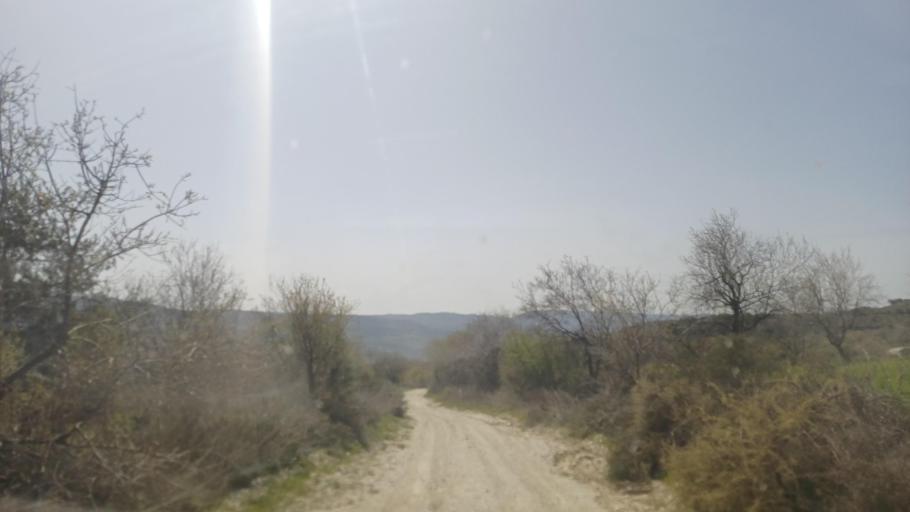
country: CY
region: Limassol
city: Pachna
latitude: 34.8695
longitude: 32.7120
